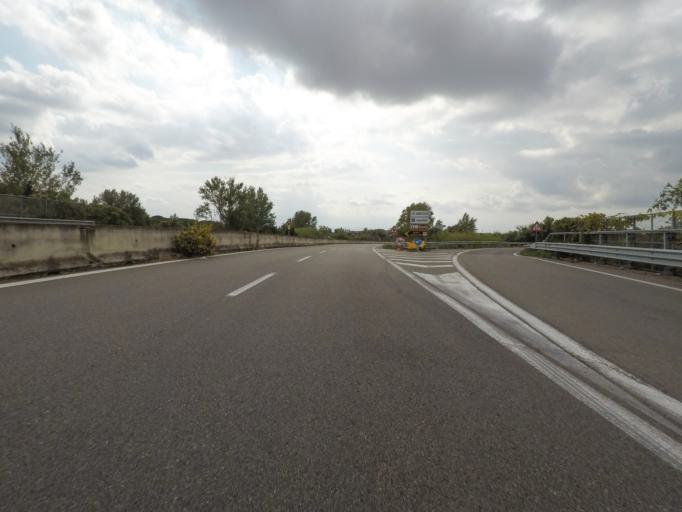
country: IT
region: Tuscany
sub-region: Provincia di Grosseto
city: Bagno Roselle
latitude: 42.8030
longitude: 11.1342
